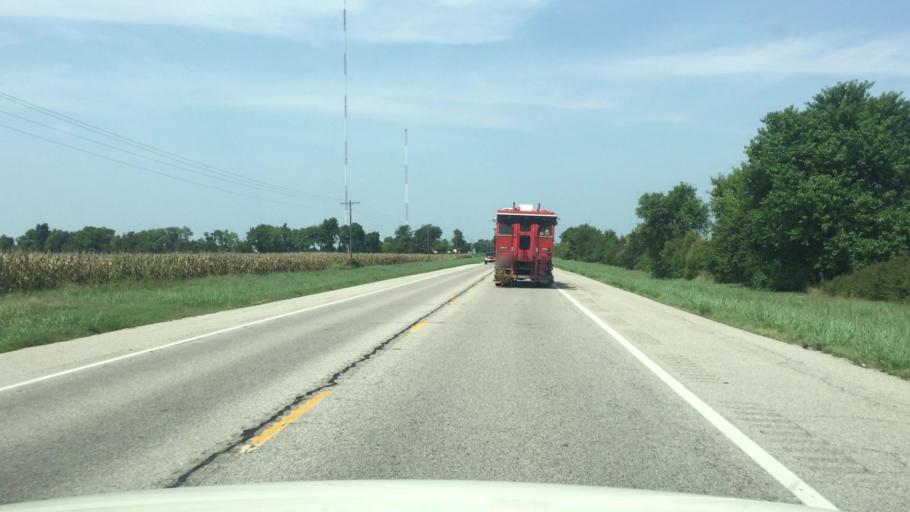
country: US
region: Missouri
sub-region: Jasper County
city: Carl Junction
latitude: 37.2109
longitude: -94.7048
